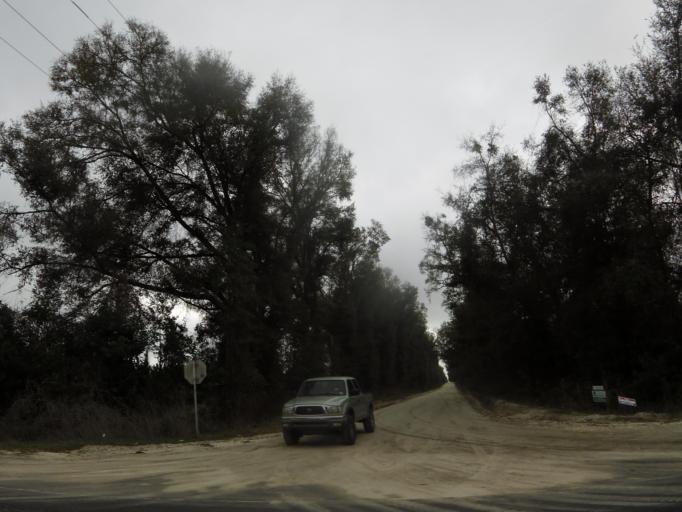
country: US
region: Florida
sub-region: Alachua County
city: High Springs
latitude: 29.8203
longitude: -82.6746
